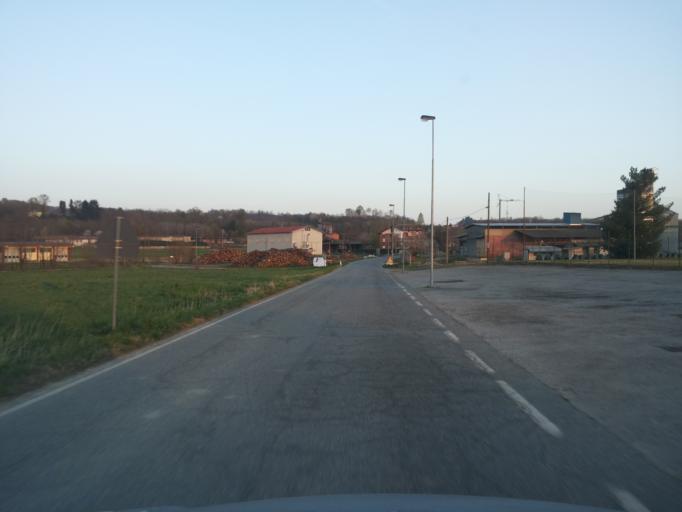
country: IT
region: Piedmont
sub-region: Provincia di Torino
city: Borgomasino
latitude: 45.3587
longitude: 7.9909
